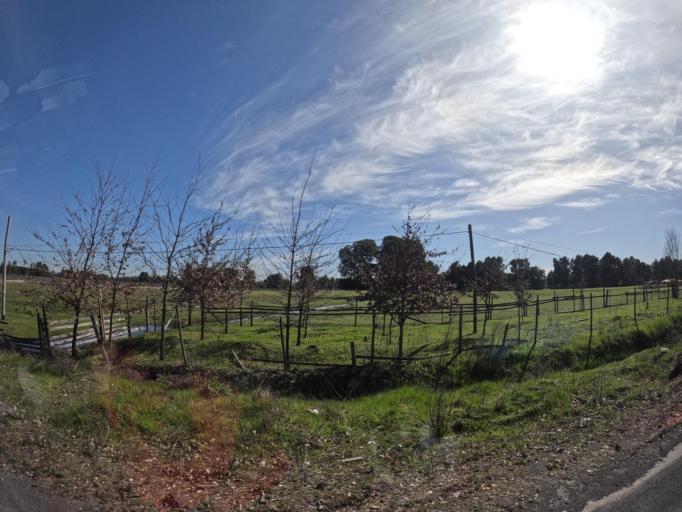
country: CL
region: Biobio
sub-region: Provincia de Biobio
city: Cabrero
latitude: -37.0321
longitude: -72.3707
